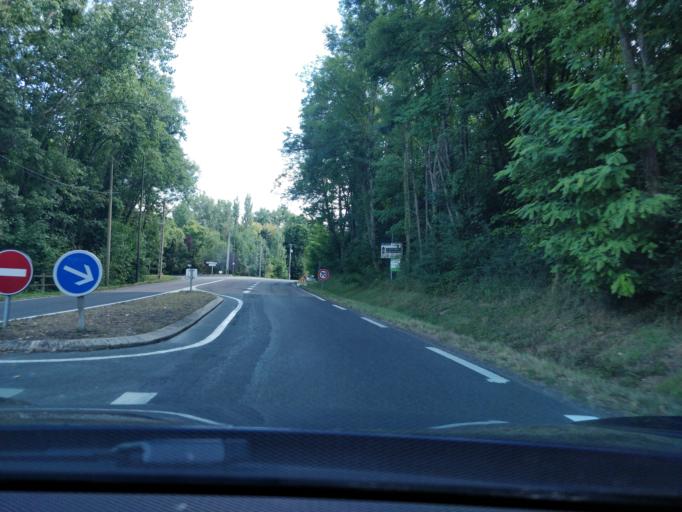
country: FR
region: Ile-de-France
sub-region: Departement de l'Essonne
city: Etampes
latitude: 48.4171
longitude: 2.1481
